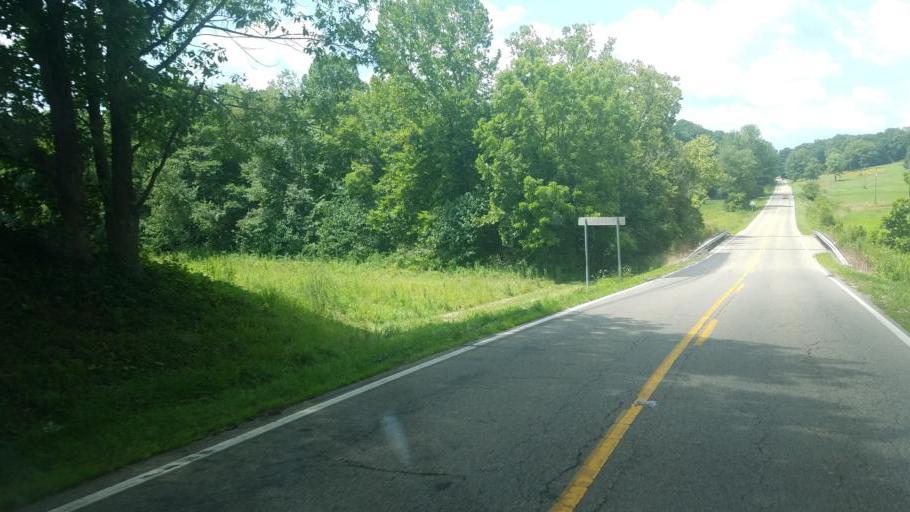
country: US
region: Ohio
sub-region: Ross County
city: Chillicothe
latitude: 39.2807
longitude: -82.7745
